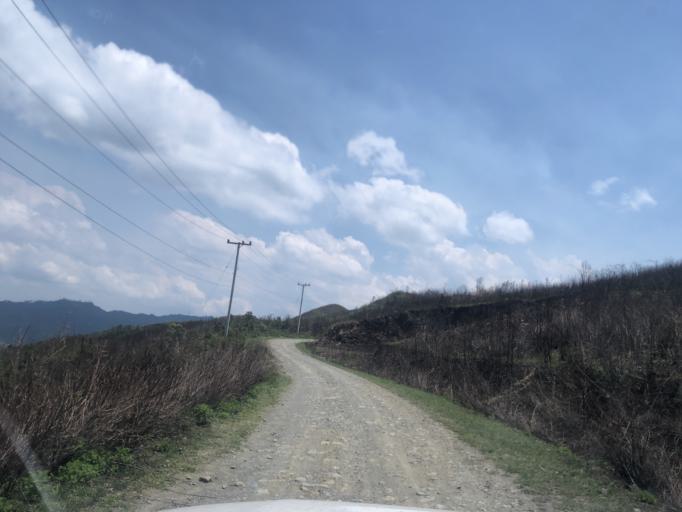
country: LA
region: Phongsali
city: Phongsali
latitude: 21.4169
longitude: 102.1850
